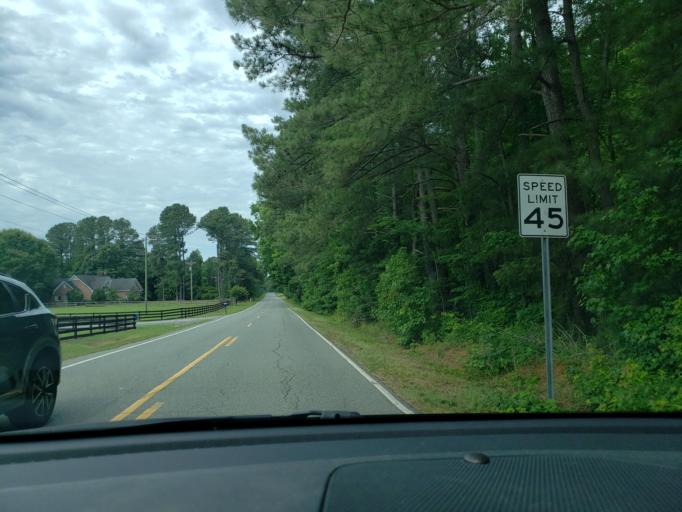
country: US
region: North Carolina
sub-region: Wake County
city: Green Level
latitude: 35.7946
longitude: -78.9837
